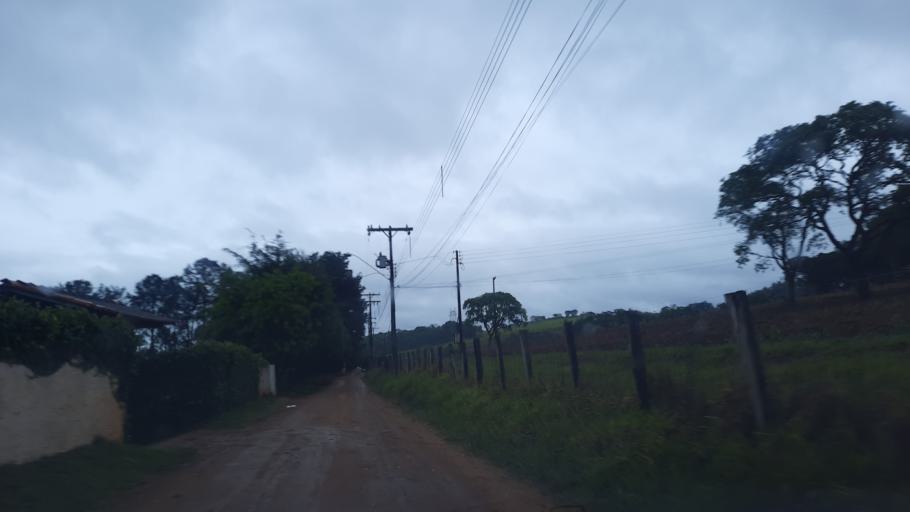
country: BR
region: Sao Paulo
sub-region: Atibaia
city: Atibaia
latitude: -23.0720
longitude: -46.5072
